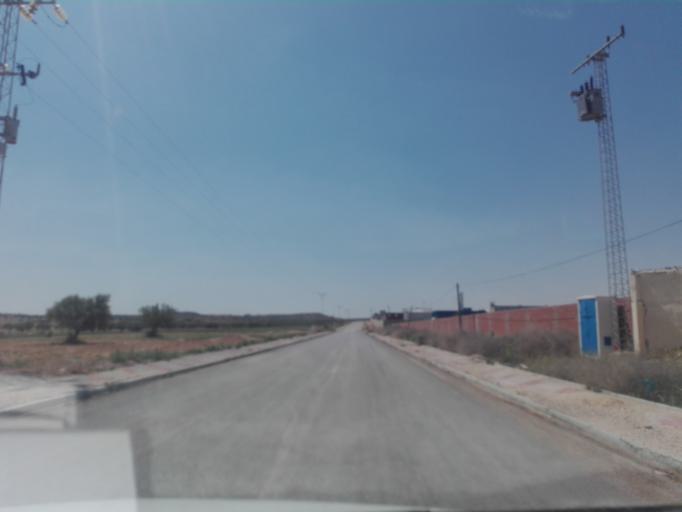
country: TN
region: Safaqis
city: Sfax
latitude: 34.7277
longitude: 10.5236
